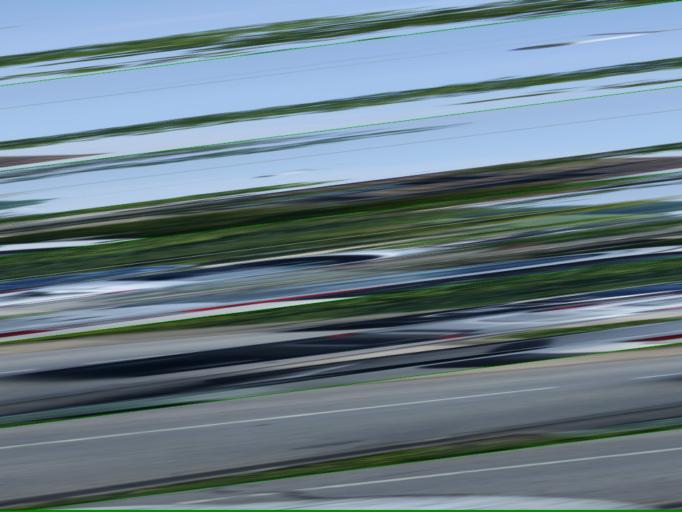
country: FR
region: Ile-de-France
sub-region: Departement des Yvelines
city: Magnanville
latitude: 48.9391
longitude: 1.6912
